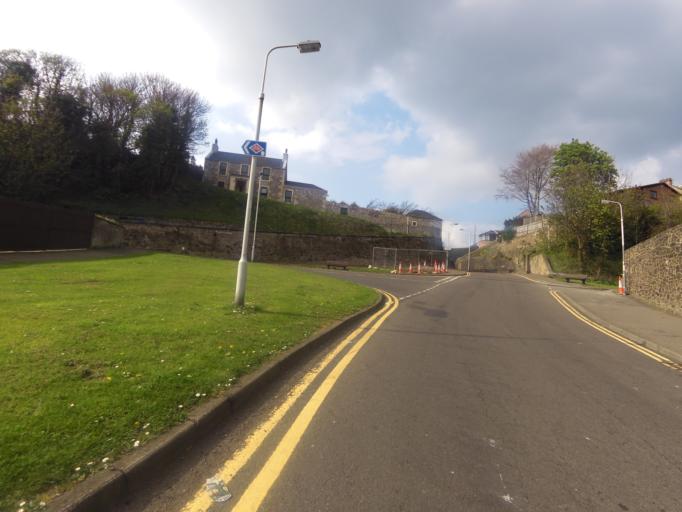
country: GB
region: Scotland
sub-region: Fife
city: Burntisland
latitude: 56.0594
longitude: -3.2358
